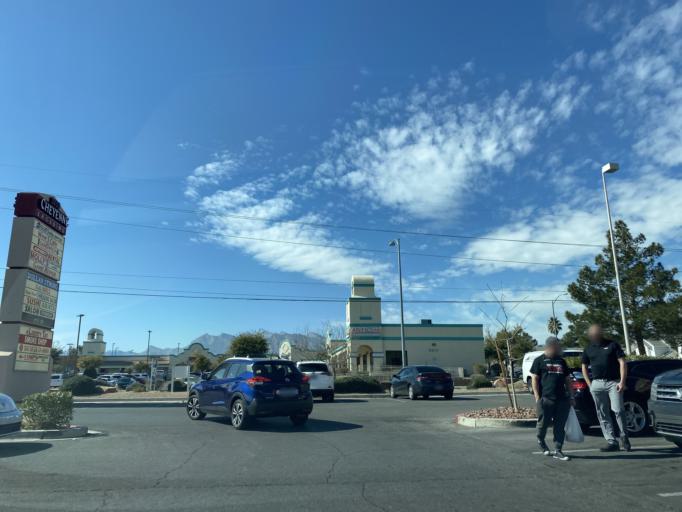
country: US
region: Nevada
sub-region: Clark County
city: Spring Valley
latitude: 36.2197
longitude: -115.2509
